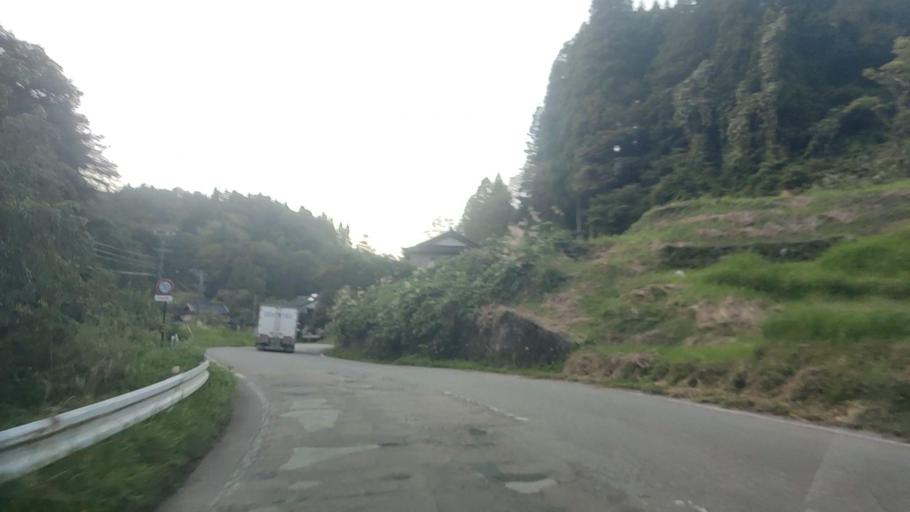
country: JP
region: Ishikawa
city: Tsubata
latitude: 36.6388
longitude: 136.7687
